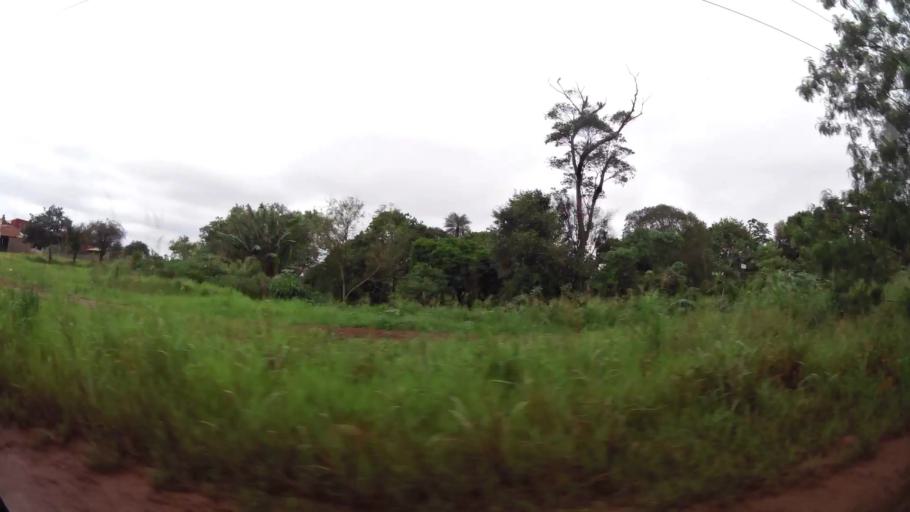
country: PY
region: Alto Parana
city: Presidente Franco
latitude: -25.5148
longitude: -54.6814
